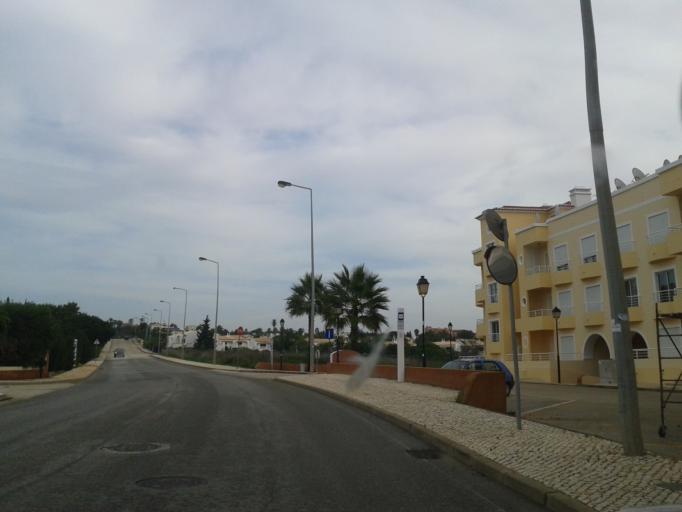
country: PT
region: Faro
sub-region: Lagos
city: Lagos
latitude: 37.0870
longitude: -8.7372
